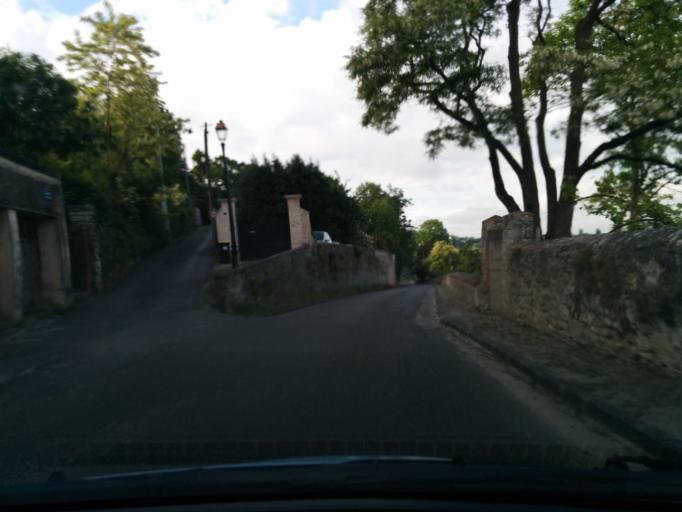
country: FR
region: Ile-de-France
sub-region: Departement des Yvelines
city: Follainville-Dennemont
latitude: 49.0612
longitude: 1.7010
